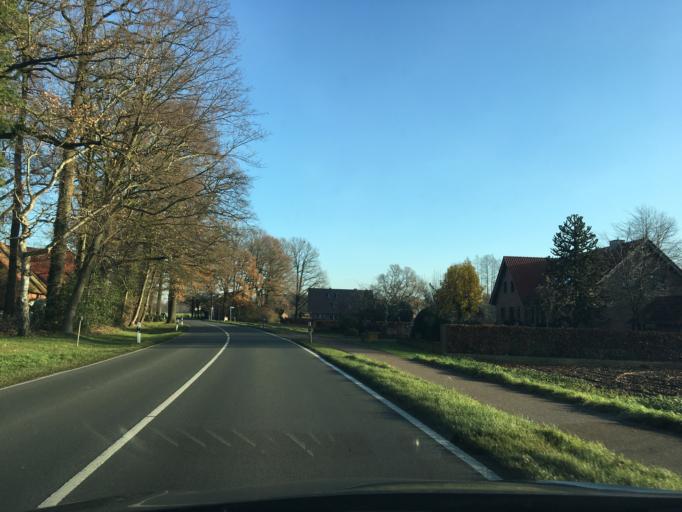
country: DE
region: North Rhine-Westphalia
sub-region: Regierungsbezirk Munster
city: Ahaus
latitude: 52.1193
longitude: 6.9254
